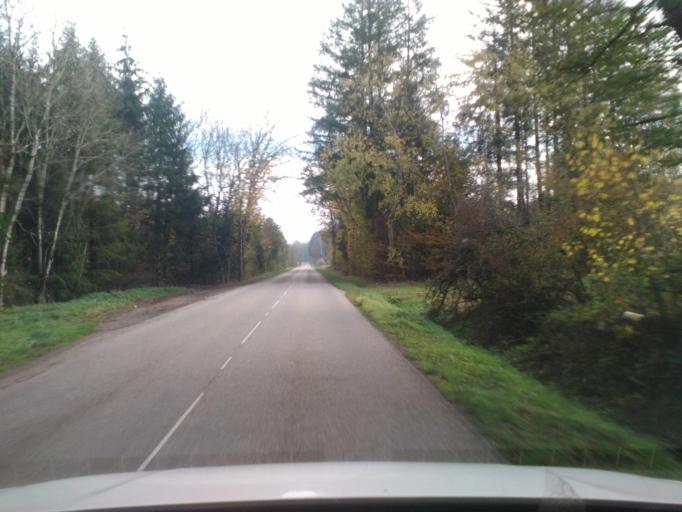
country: FR
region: Lorraine
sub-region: Departement des Vosges
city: Saint-Michel-sur-Meurthe
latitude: 48.3437
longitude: 6.9045
